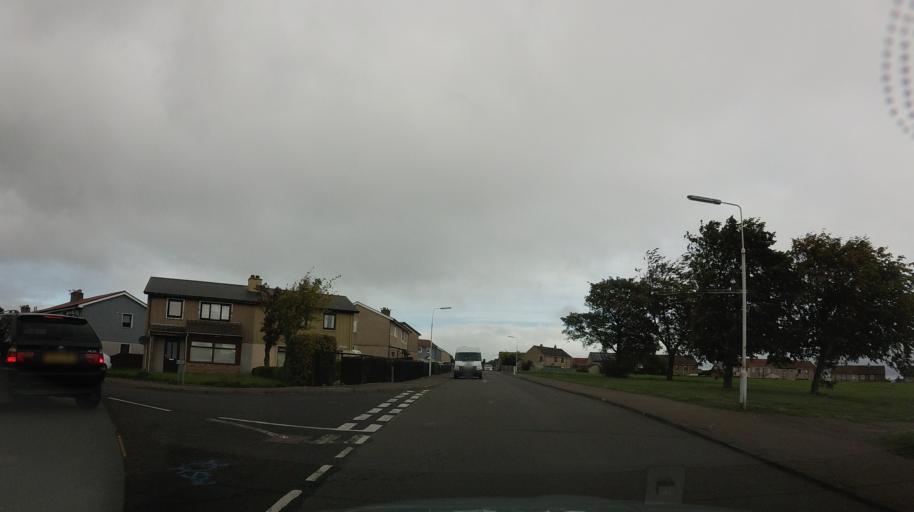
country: GB
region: Scotland
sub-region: Fife
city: Cowdenbeath
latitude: 56.1046
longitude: -3.3573
